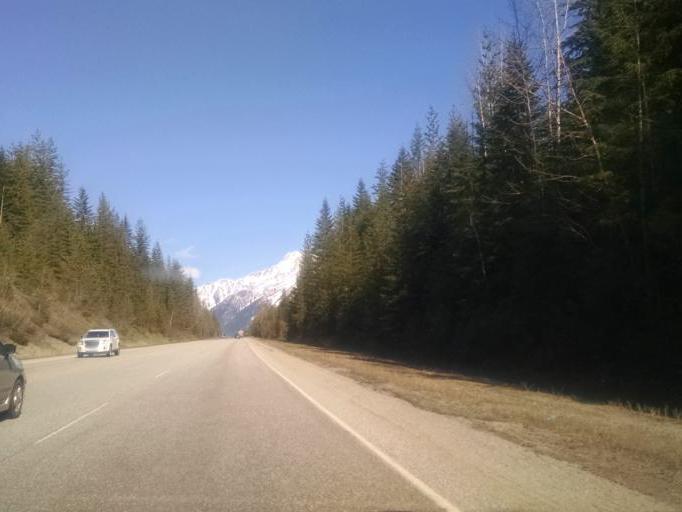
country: CA
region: British Columbia
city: Revelstoke
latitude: 51.0173
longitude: -118.0799
